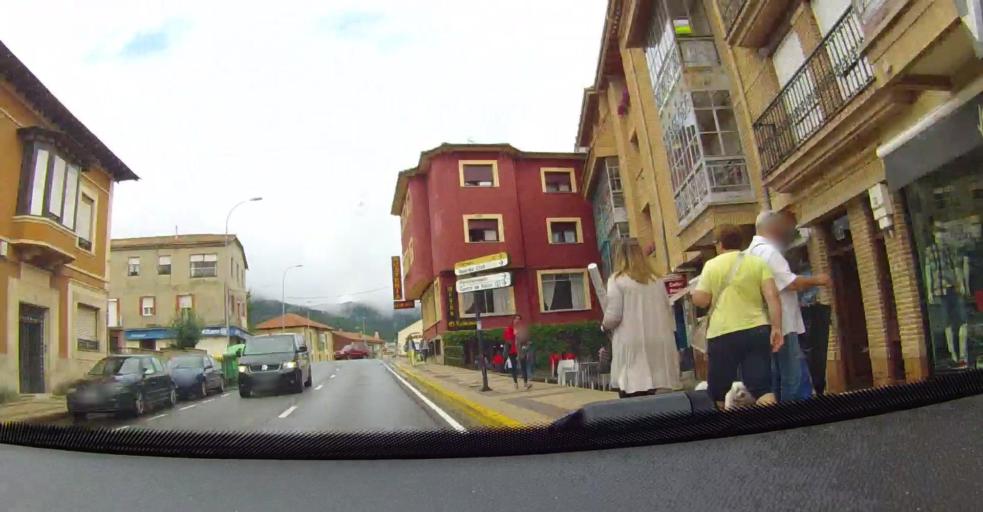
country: ES
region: Castille and Leon
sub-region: Provincia de Leon
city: Bonar
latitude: 42.8664
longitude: -5.3235
